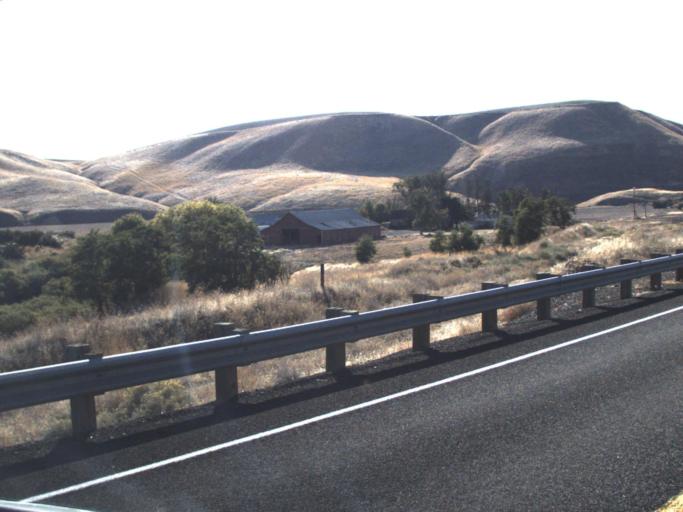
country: US
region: Washington
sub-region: Walla Walla County
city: Garrett
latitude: 46.2901
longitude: -118.5055
